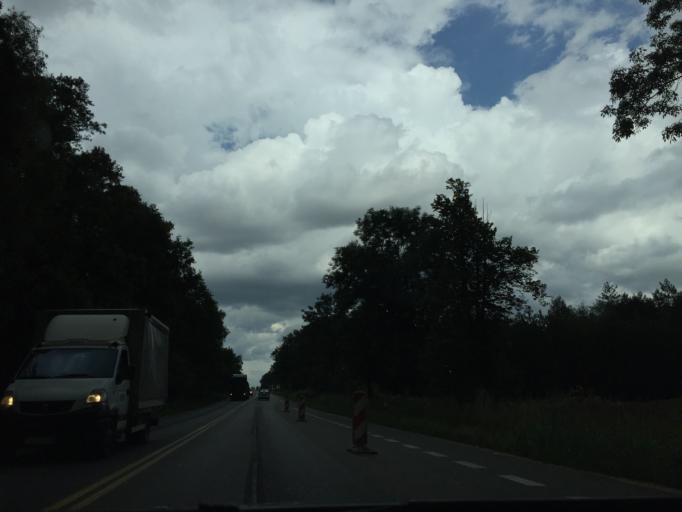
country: PL
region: Swietokrzyskie
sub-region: Powiat jedrzejowski
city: Jedrzejow
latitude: 50.6872
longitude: 20.3584
